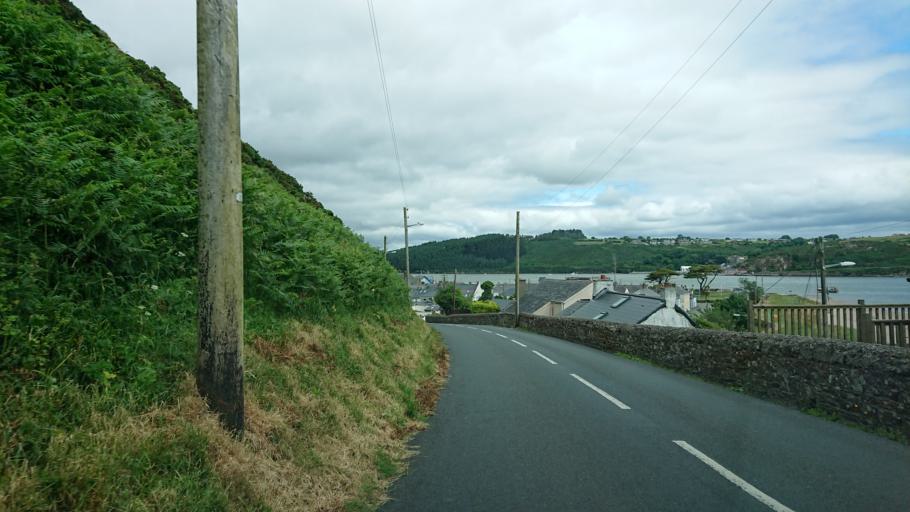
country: IE
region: Munster
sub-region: Waterford
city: Dunmore East
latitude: 52.2369
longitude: -6.9719
